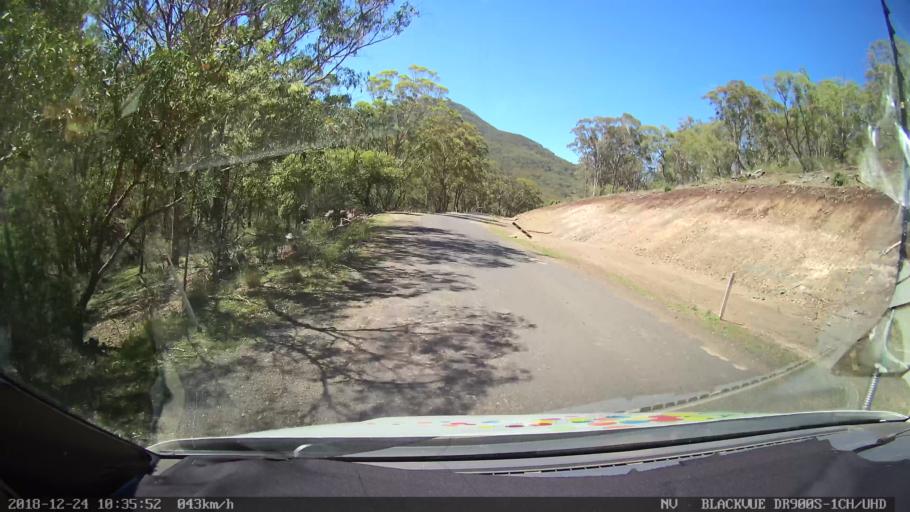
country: AU
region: New South Wales
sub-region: Upper Hunter Shire
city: Merriwa
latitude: -31.8411
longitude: 150.5012
